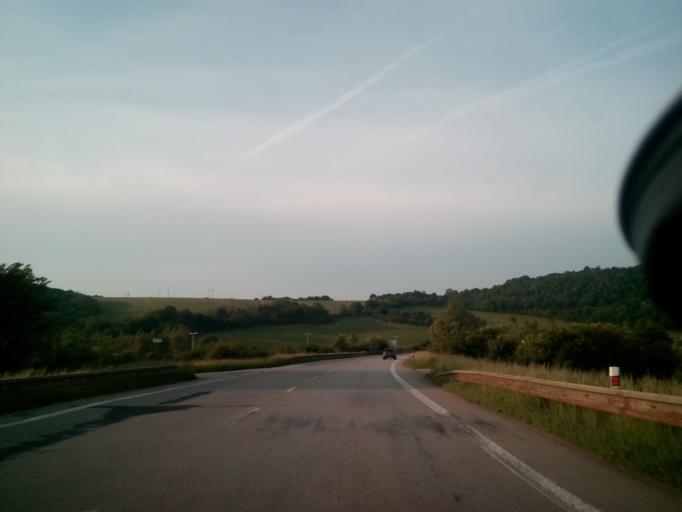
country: SK
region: Kosicky
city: Roznava
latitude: 48.5361
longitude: 20.3960
